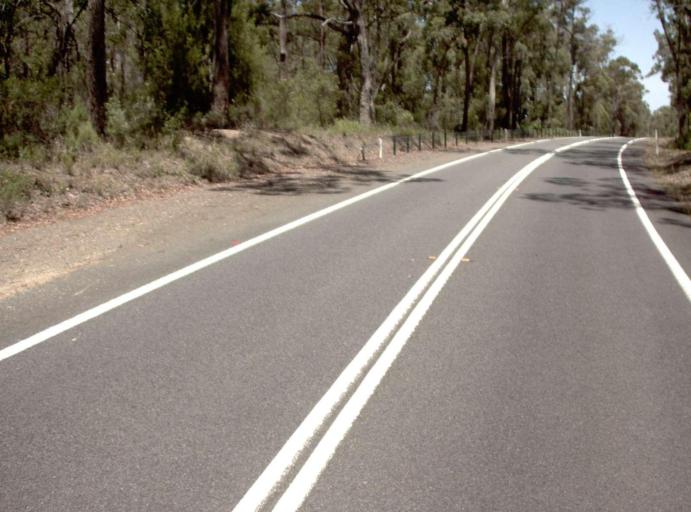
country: AU
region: Victoria
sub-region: East Gippsland
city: Lakes Entrance
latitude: -37.8280
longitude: 148.0333
